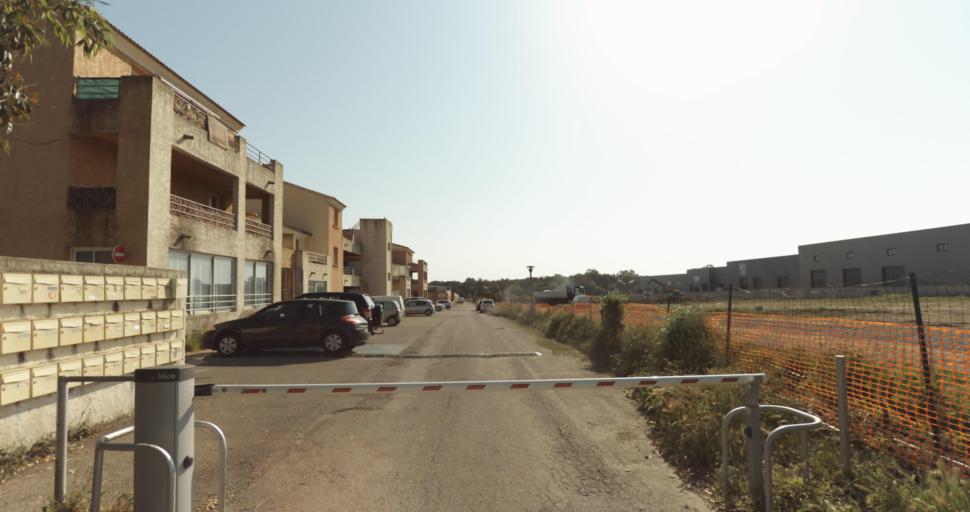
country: FR
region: Corsica
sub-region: Departement de la Haute-Corse
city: Biguglia
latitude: 42.6338
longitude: 9.4352
